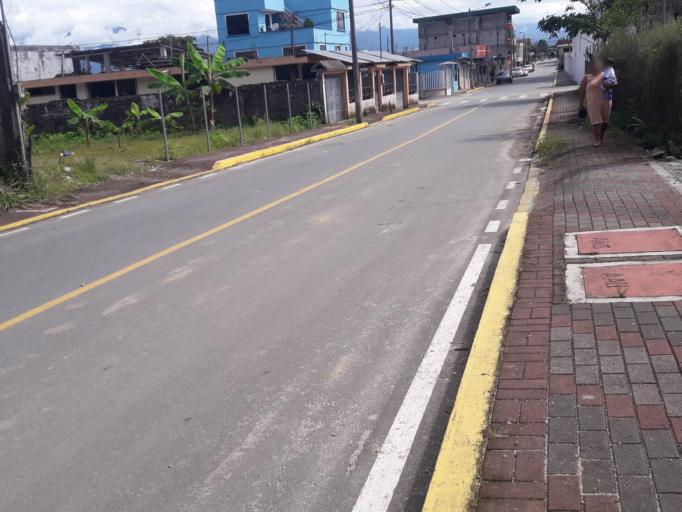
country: EC
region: Napo
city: Tena
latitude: -1.0095
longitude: -77.8145
